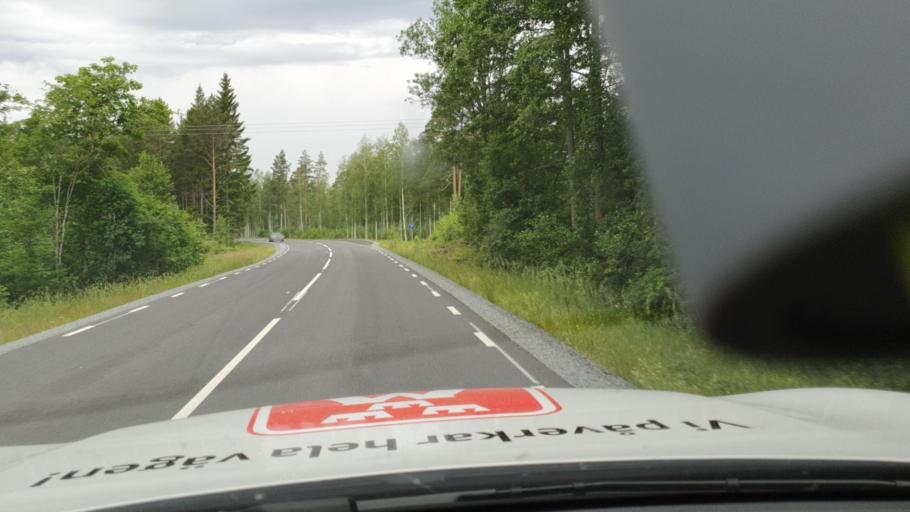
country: SE
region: Vaestra Goetaland
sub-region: Gullspangs Kommun
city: Anderstorp
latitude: 58.9187
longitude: 14.4424
